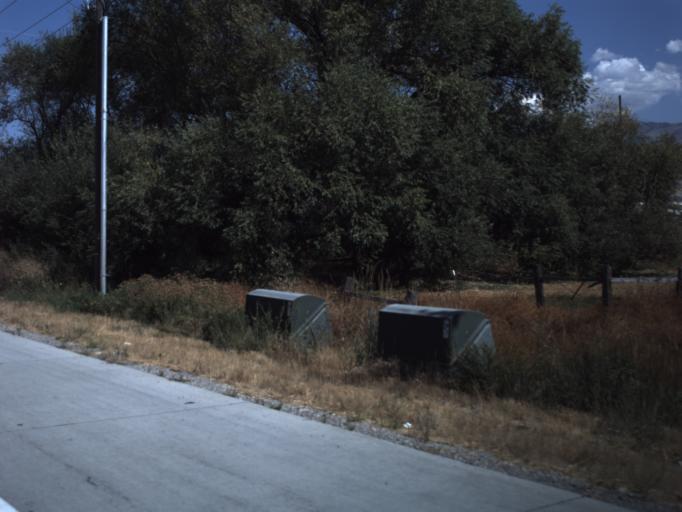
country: US
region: Utah
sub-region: Cache County
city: Logan
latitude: 41.7649
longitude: -111.8586
